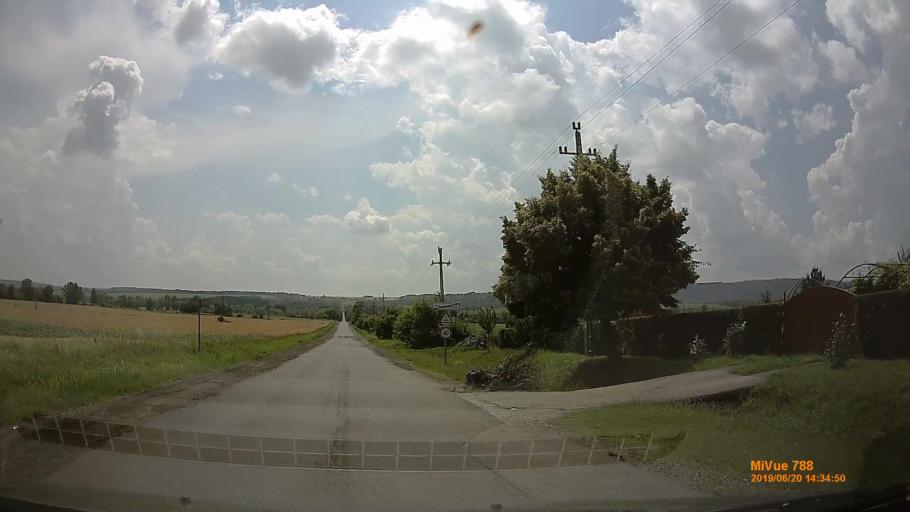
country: HU
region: Baranya
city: Hosszuheteny
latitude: 46.1159
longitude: 18.3316
